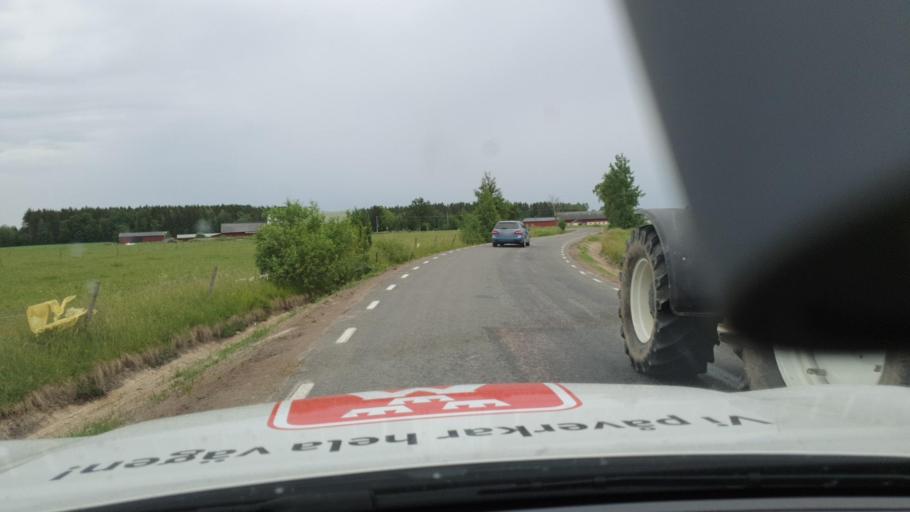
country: SE
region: Vaestra Goetaland
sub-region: Tidaholms Kommun
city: Olofstorp
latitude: 58.3173
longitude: 14.0600
